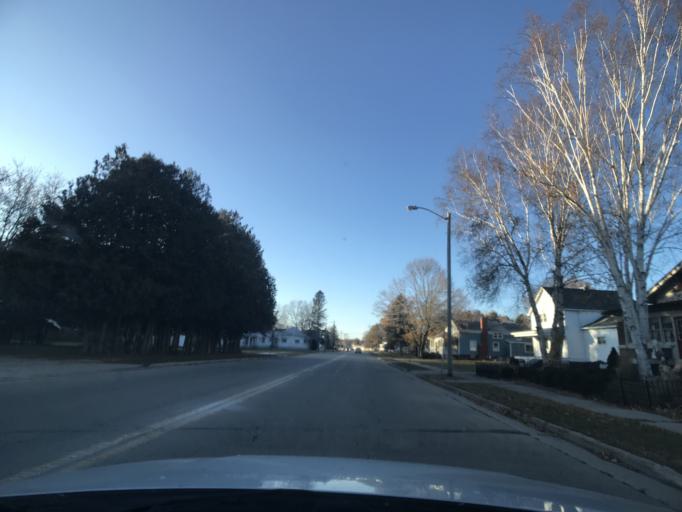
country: US
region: Wisconsin
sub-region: Oconto County
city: Oconto
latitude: 44.8910
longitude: -87.8787
